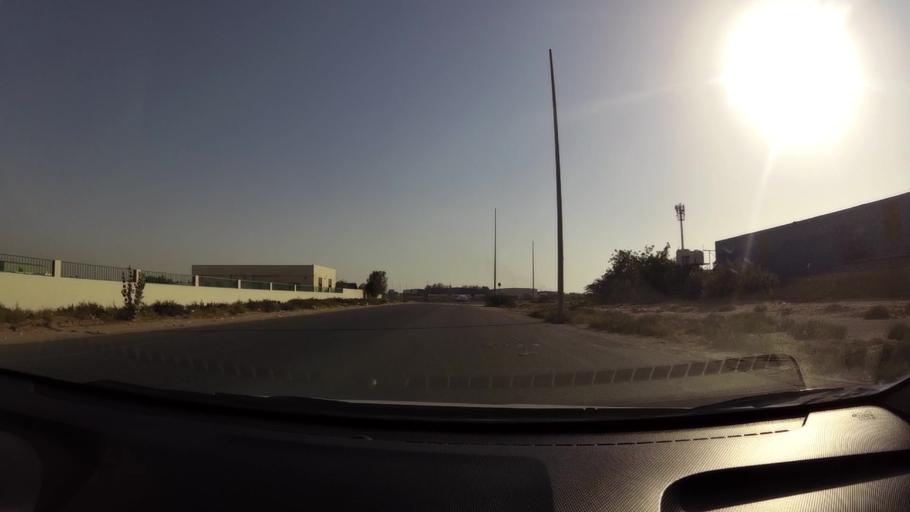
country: AE
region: Umm al Qaywayn
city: Umm al Qaywayn
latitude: 25.4484
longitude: 55.5563
